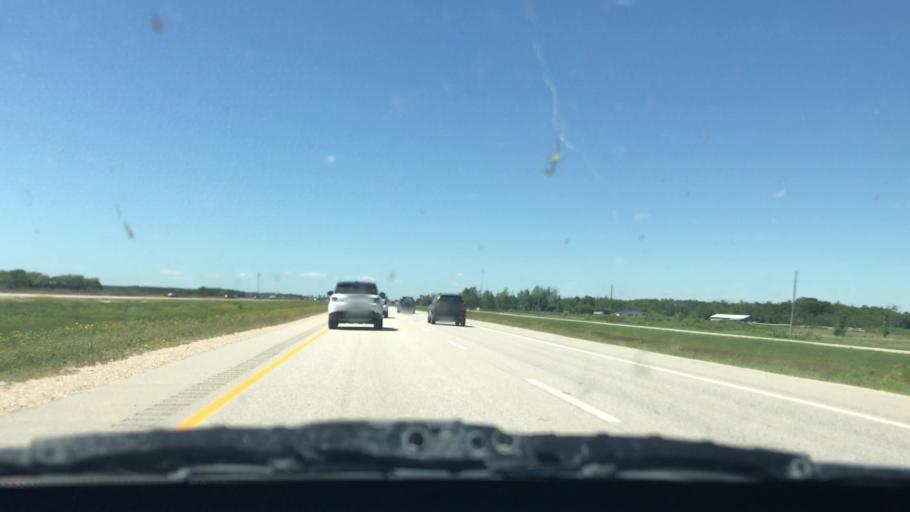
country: CA
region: Manitoba
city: Winnipeg
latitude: 49.8126
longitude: -96.9169
